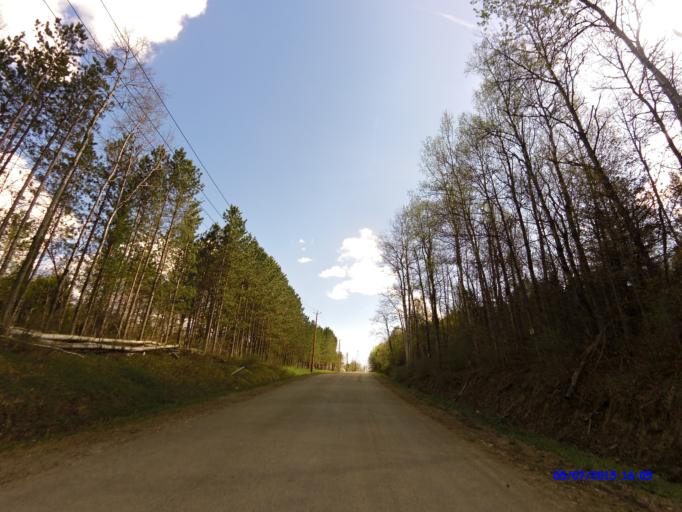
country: US
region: New York
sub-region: Cattaraugus County
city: Franklinville
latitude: 42.3055
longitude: -78.6113
